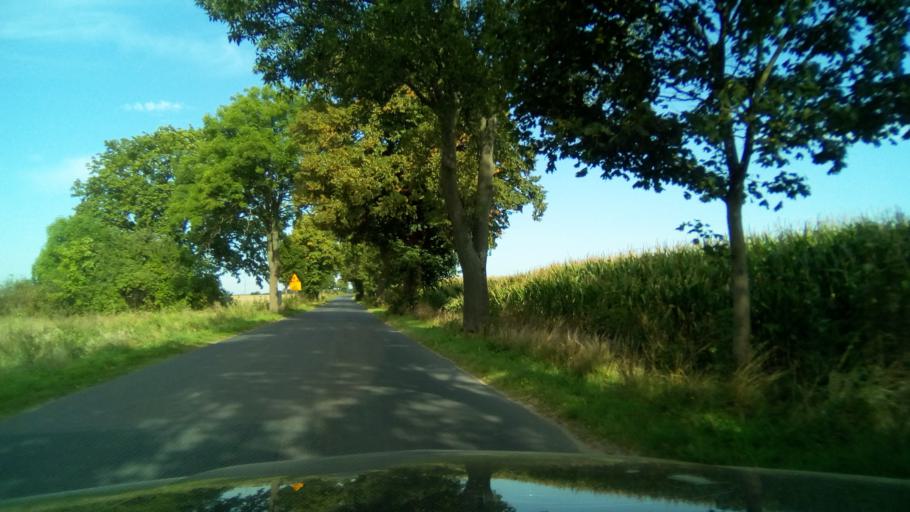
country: PL
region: Greater Poland Voivodeship
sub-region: Powiat pilski
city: Szydlowo
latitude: 53.1671
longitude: 16.6078
